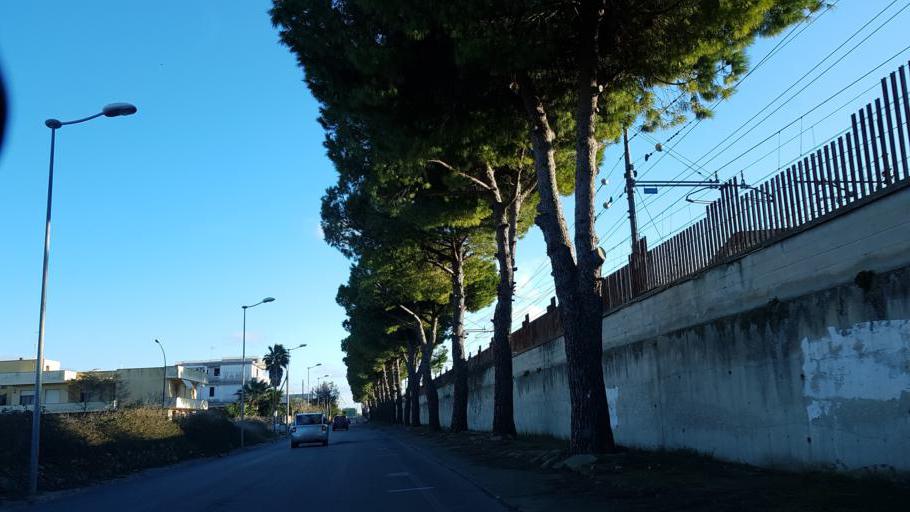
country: IT
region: Apulia
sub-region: Provincia di Lecce
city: Squinzano
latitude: 40.4372
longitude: 18.0486
